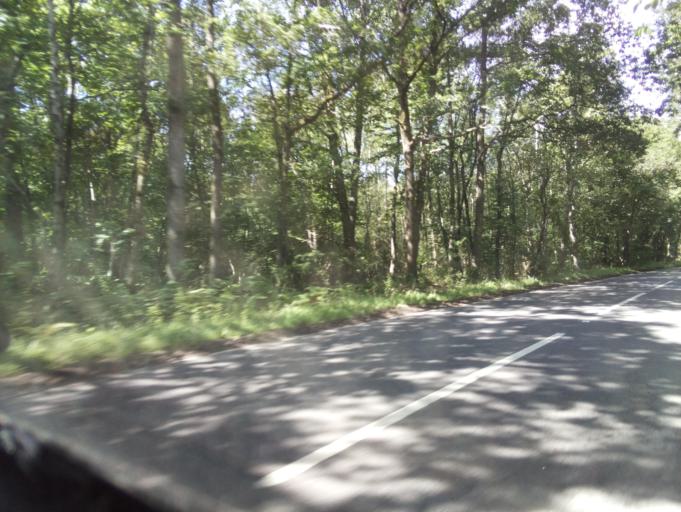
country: GB
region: England
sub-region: West Berkshire
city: Winterbourne
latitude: 51.4384
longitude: -1.3338
